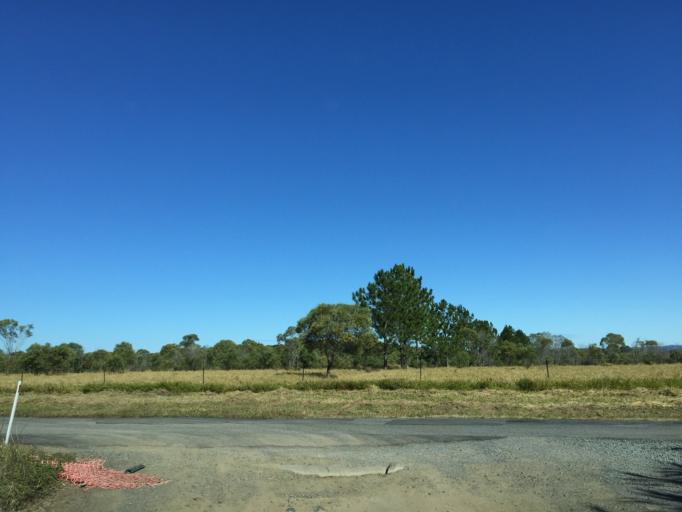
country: AU
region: Queensland
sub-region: Moreton Bay
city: Caboolture
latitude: -27.0205
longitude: 152.9854
